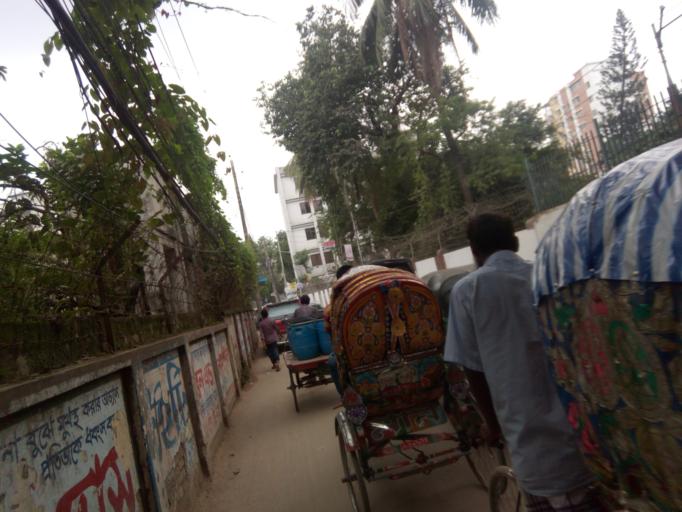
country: BD
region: Dhaka
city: Paltan
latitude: 23.7406
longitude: 90.4075
